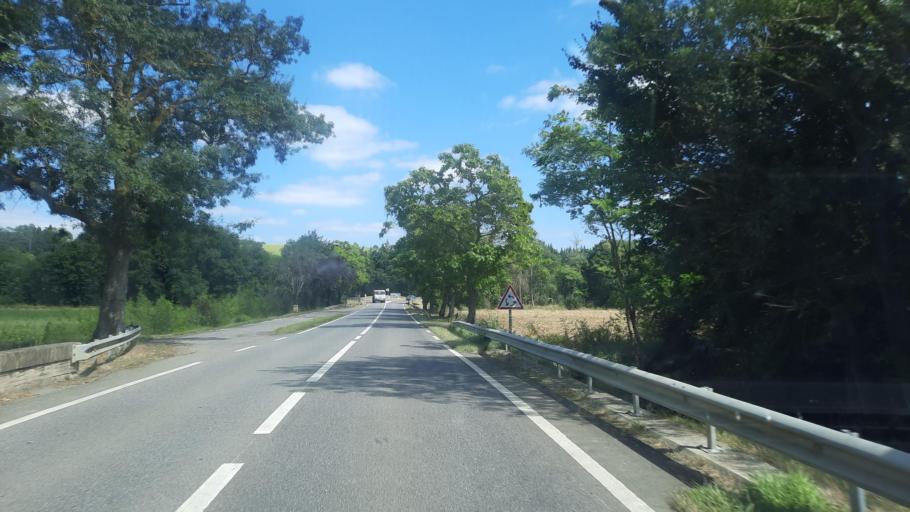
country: FR
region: Midi-Pyrenees
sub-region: Departement du Gers
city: Samatan
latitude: 43.4967
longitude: 0.9662
